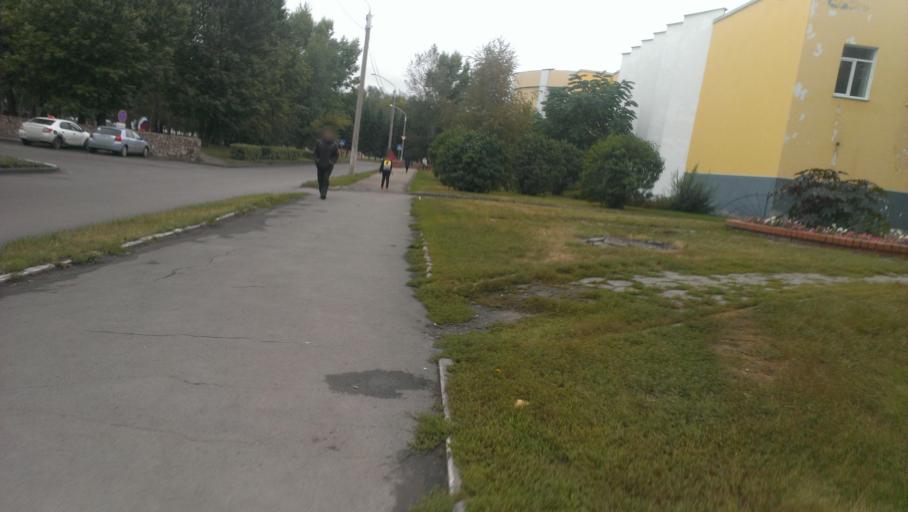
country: RU
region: Altai Krai
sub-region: Gorod Barnaulskiy
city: Barnaul
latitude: 53.3668
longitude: 83.6891
